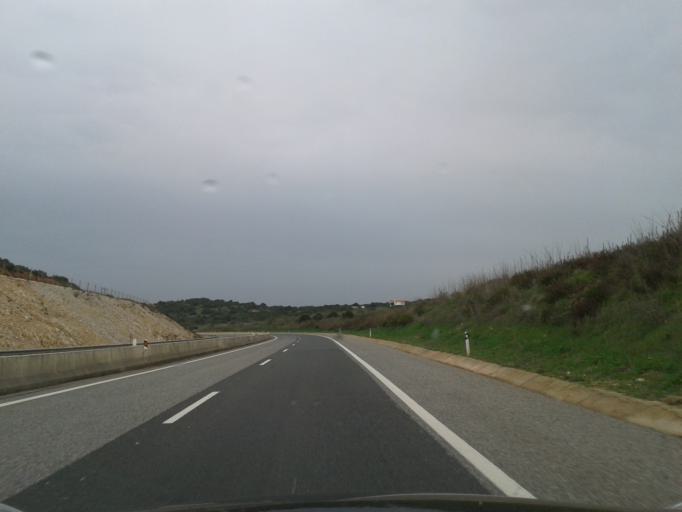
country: PT
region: Faro
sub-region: Lagos
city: Lagos
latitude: 37.1298
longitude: -8.7110
